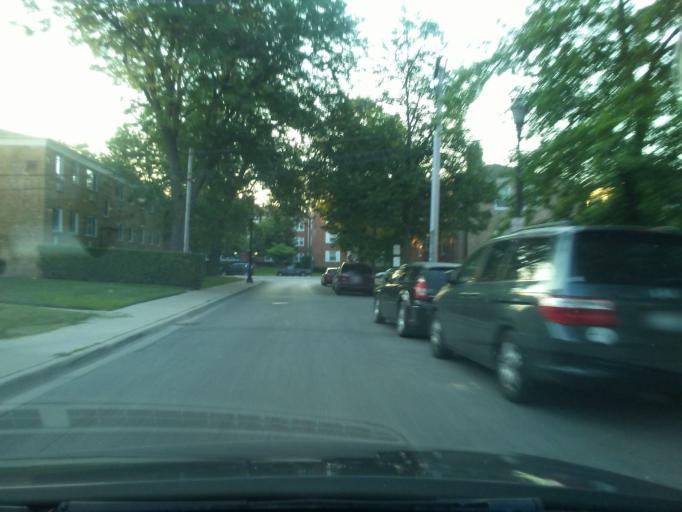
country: US
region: Illinois
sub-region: Cook County
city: Evanston
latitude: 42.0255
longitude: -87.6813
